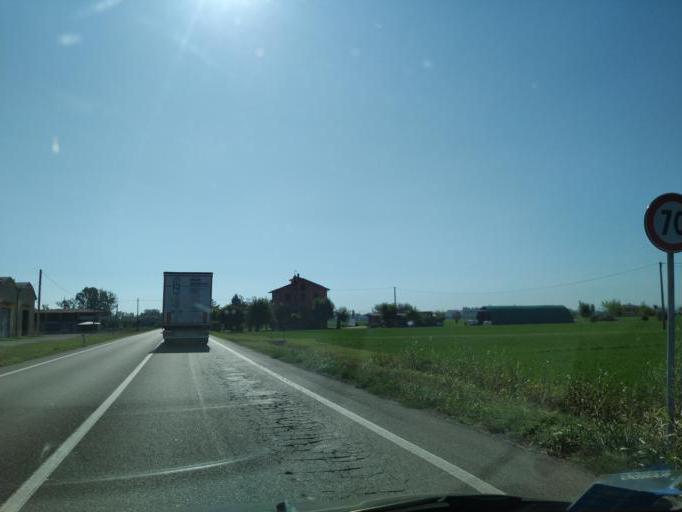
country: IT
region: Emilia-Romagna
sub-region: Provincia di Bologna
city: Sant'Agata Bolognese
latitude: 44.6495
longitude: 11.1580
